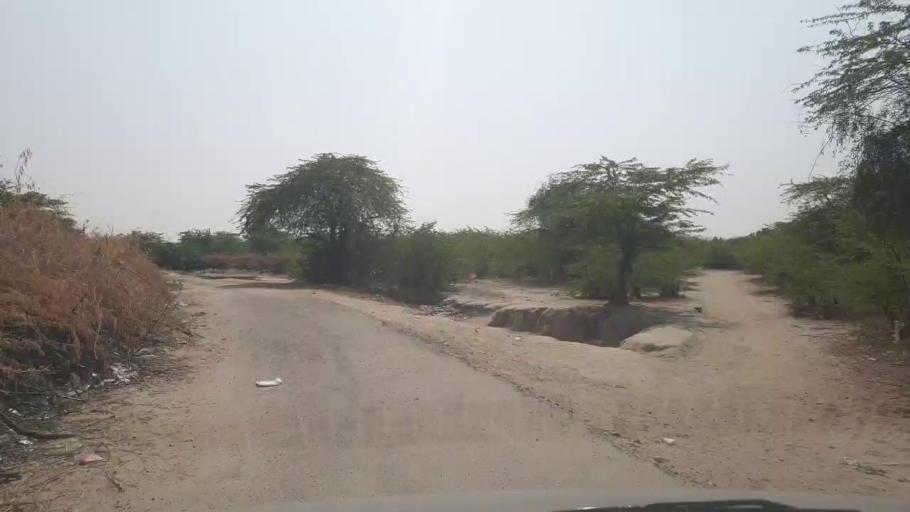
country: PK
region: Sindh
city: Chor
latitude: 25.4873
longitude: 69.7830
